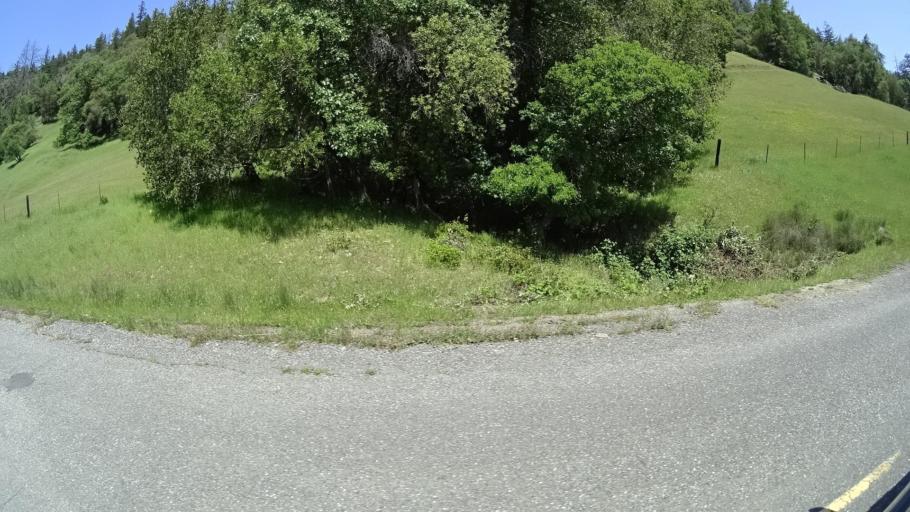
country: US
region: California
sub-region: Humboldt County
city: Redway
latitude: 40.2262
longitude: -123.6414
